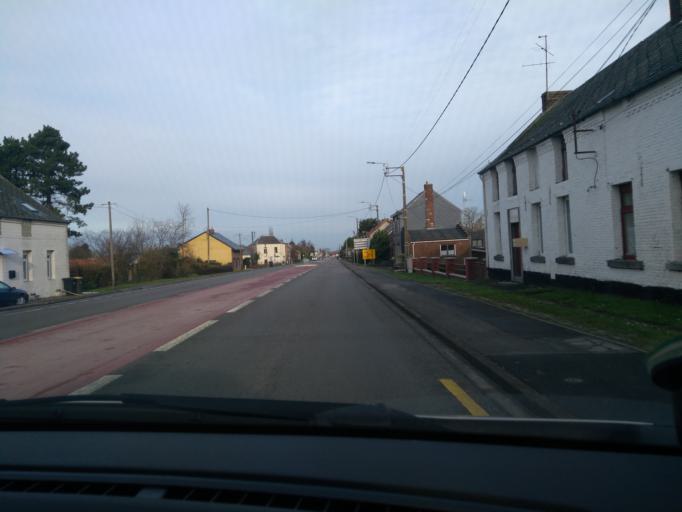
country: FR
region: Nord-Pas-de-Calais
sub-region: Departement du Nord
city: Maubeuge
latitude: 50.3315
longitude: 3.9737
